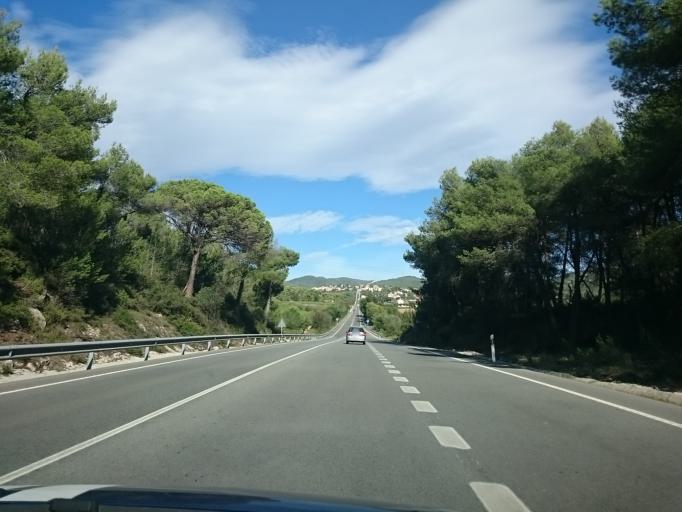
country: ES
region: Catalonia
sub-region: Provincia de Barcelona
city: Subirats
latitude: 41.3908
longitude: 1.8288
